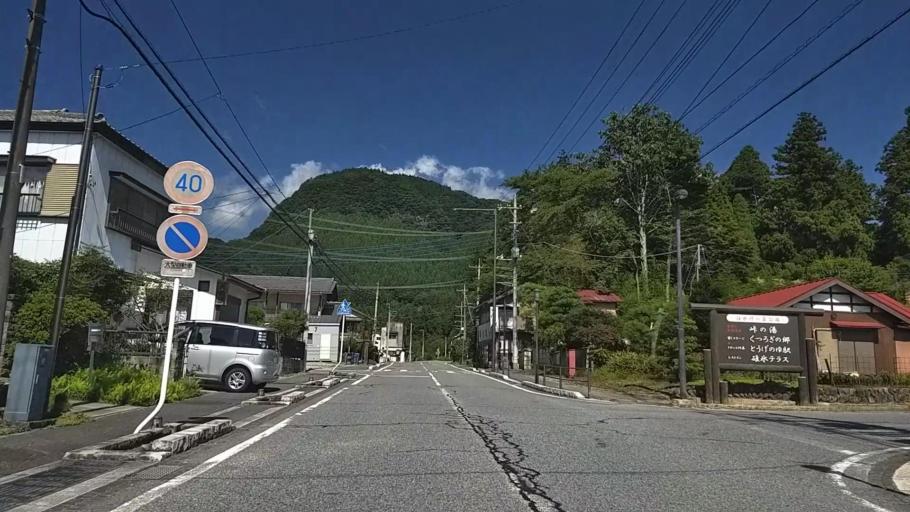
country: JP
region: Gunma
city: Annaka
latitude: 36.3512
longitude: 138.7159
